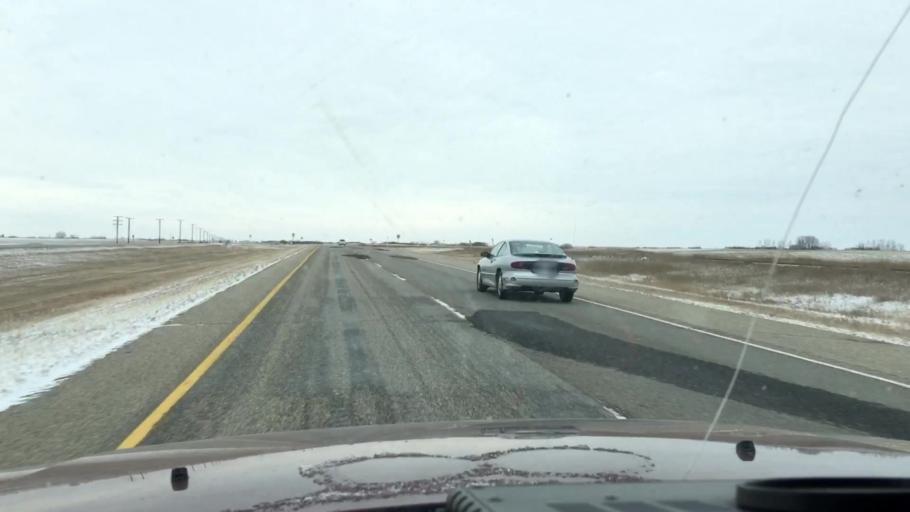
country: CA
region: Saskatchewan
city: Watrous
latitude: 51.4183
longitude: -106.1918
